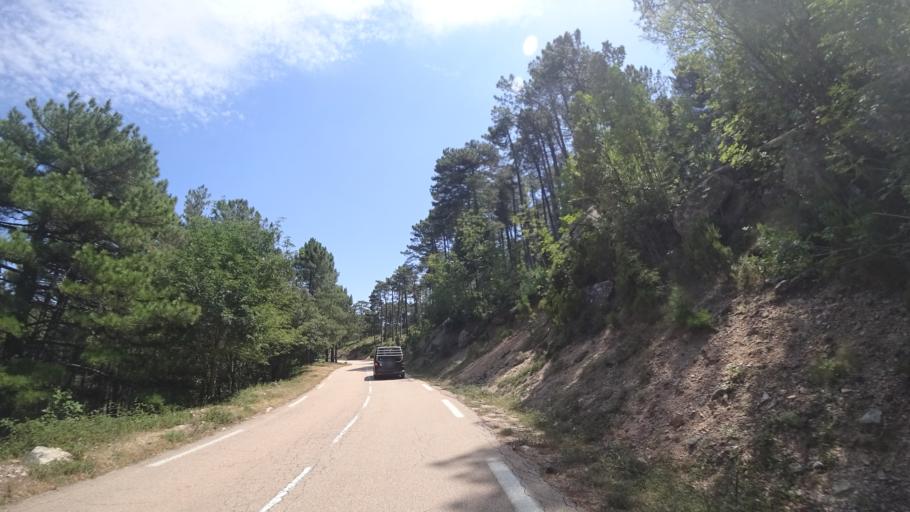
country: FR
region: Corsica
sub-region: Departement de la Corse-du-Sud
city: Zonza
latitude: 41.6767
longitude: 9.2043
